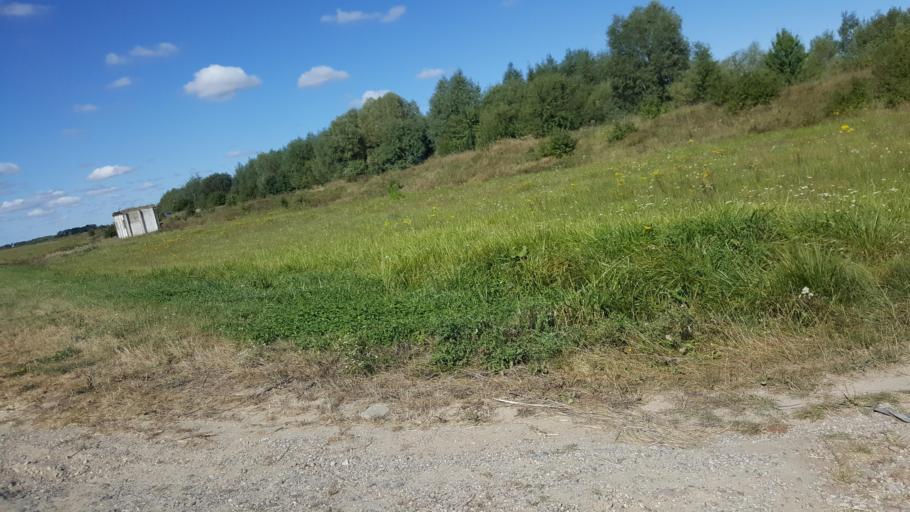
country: BY
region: Brest
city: Vysokaye
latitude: 52.3671
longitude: 23.5339
